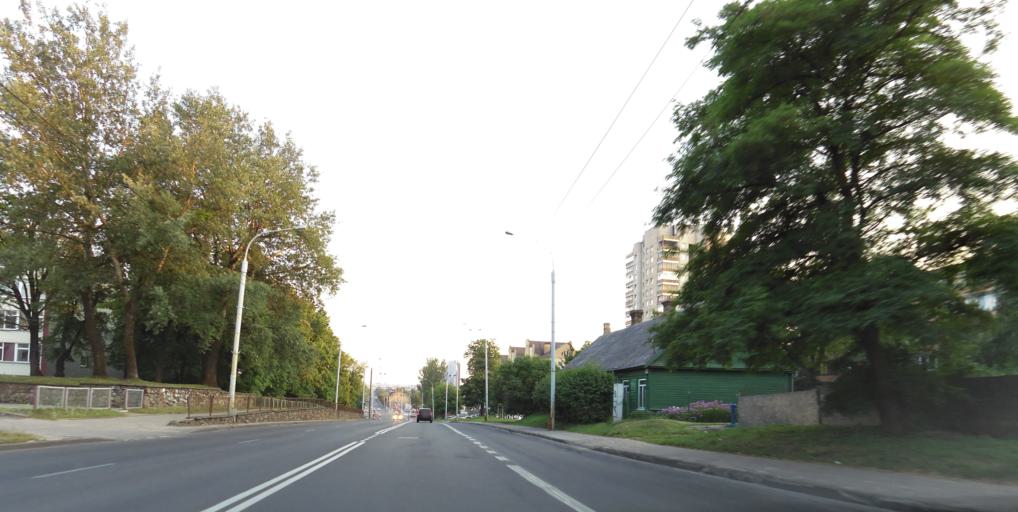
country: LT
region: Vilnius County
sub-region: Vilnius
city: Vilnius
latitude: 54.7065
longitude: 25.2847
